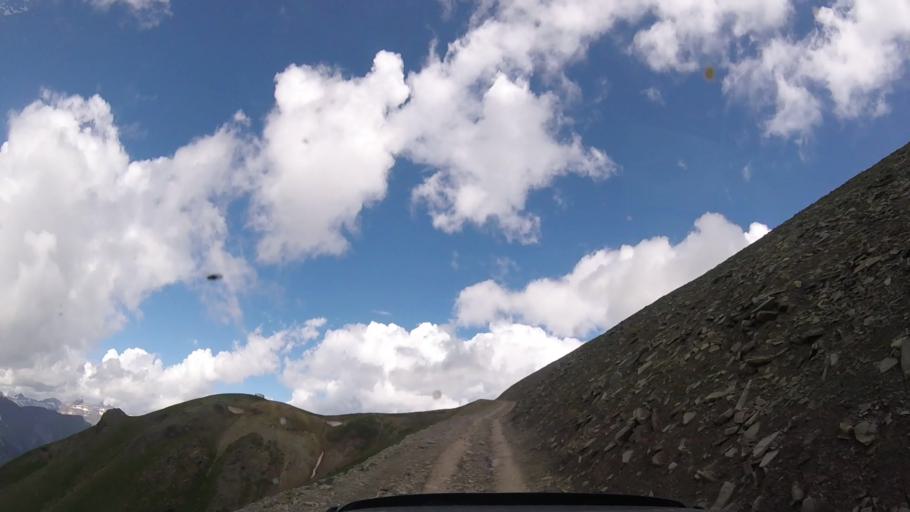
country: US
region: Colorado
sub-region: Ouray County
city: Ouray
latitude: 37.9685
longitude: -107.5895
